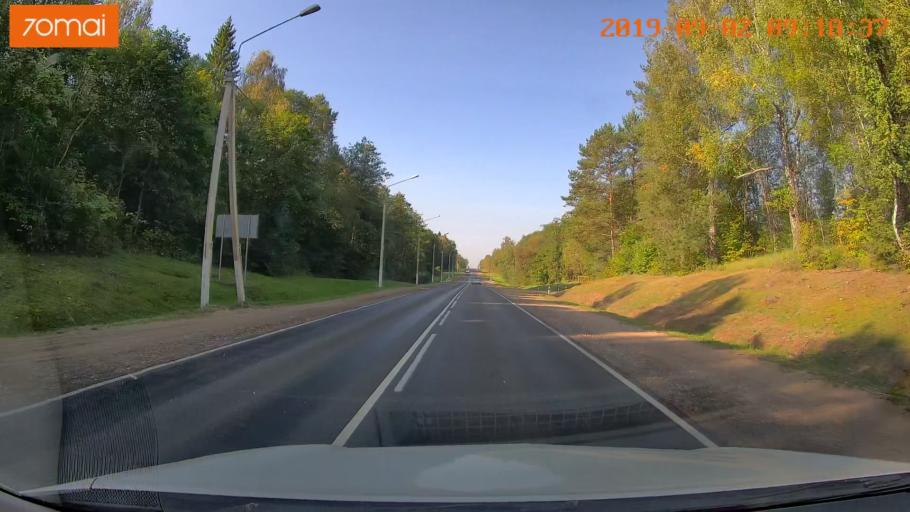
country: RU
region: Kaluga
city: Nikola-Lenivets
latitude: 54.8144
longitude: 35.4235
